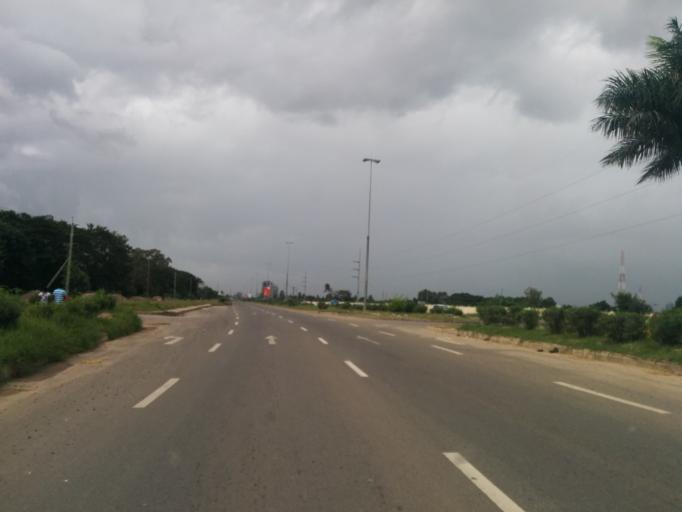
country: TZ
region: Dar es Salaam
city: Magomeni
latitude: -6.7833
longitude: 39.2139
